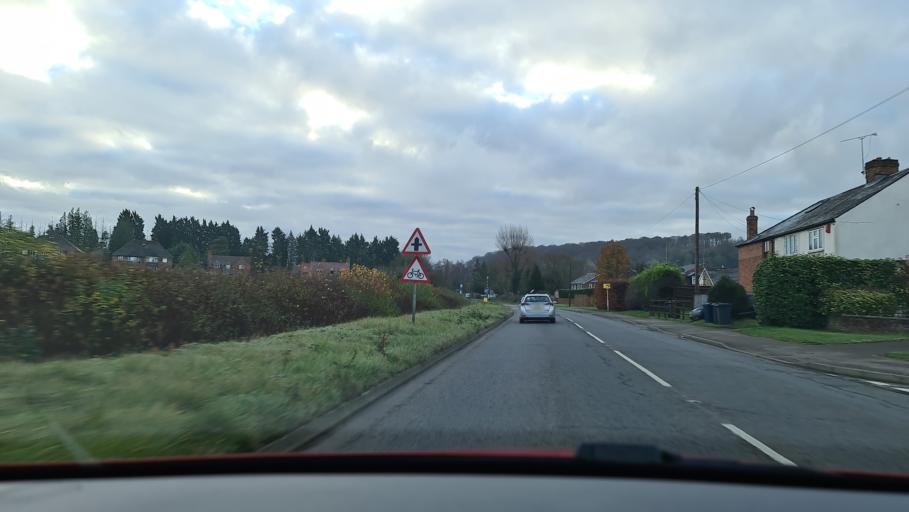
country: GB
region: England
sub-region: Buckinghamshire
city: Princes Risborough
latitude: 51.6769
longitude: -0.8247
